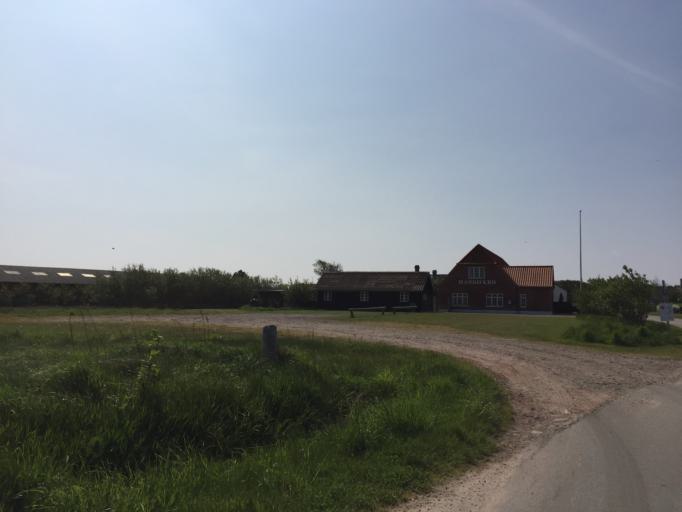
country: DK
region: South Denmark
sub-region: Esbjerg Kommune
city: Tjaereborg
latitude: 55.2772
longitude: 8.5370
